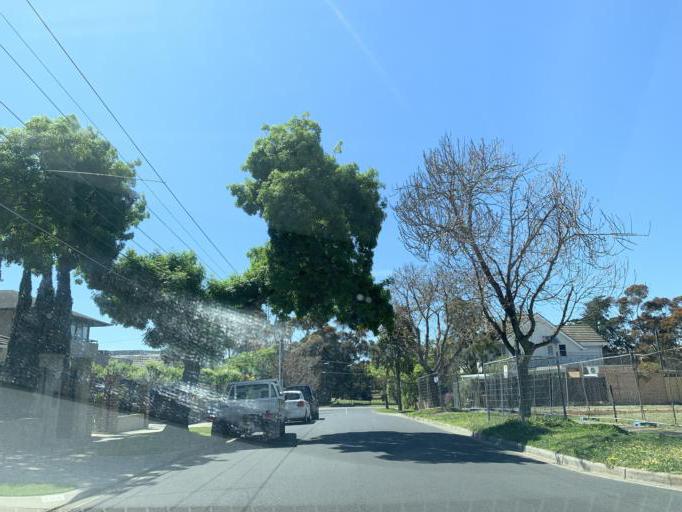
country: AU
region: Victoria
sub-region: Bayside
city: Hampton
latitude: -37.9281
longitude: 145.0138
